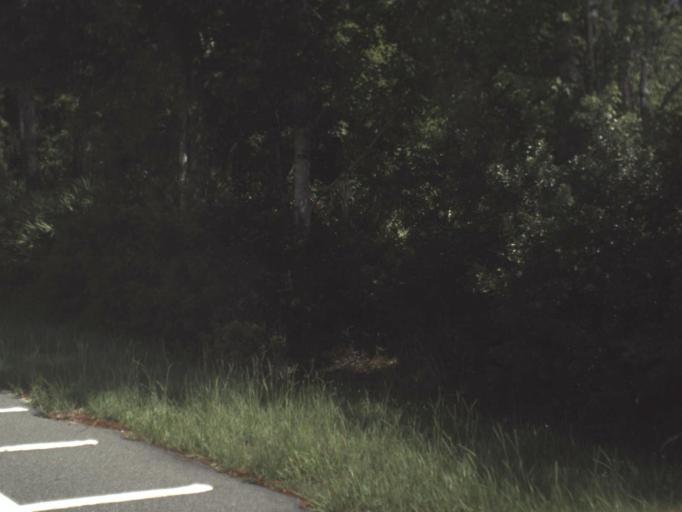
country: US
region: Florida
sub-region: Putnam County
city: Palatka
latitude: 29.6869
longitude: -81.7391
